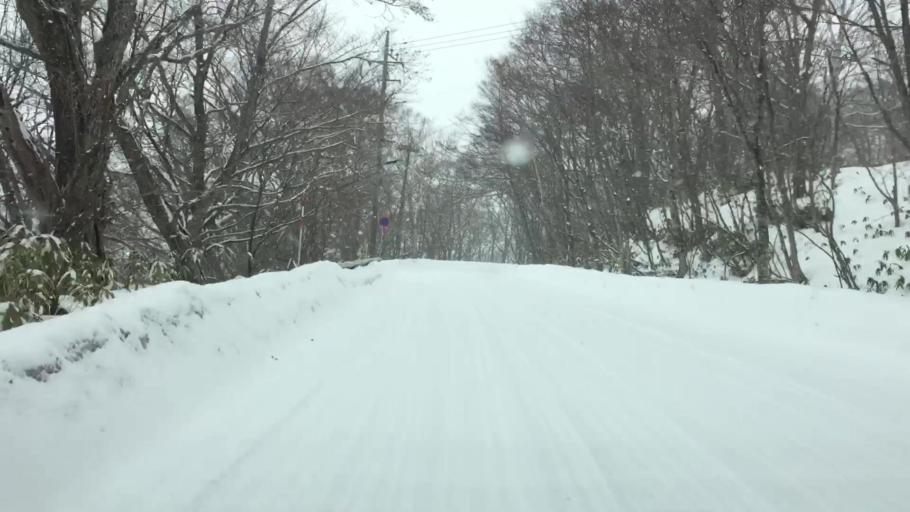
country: JP
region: Tochigi
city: Nikko
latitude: 36.9200
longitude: 139.7401
